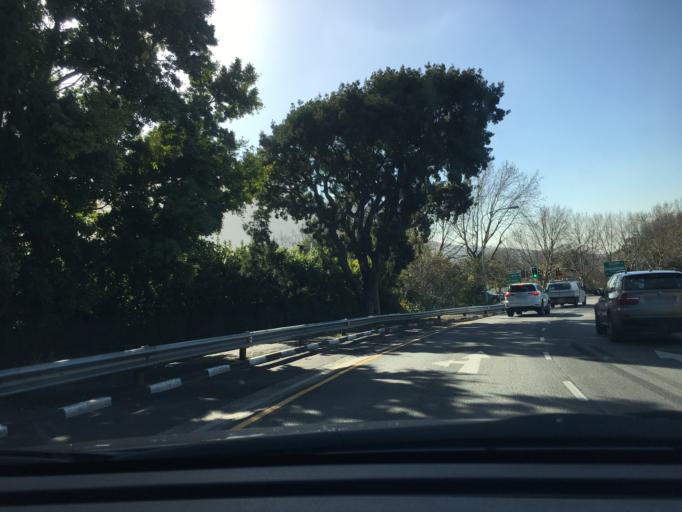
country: ZA
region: Western Cape
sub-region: City of Cape Town
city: Newlands
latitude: -33.9863
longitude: 18.4515
